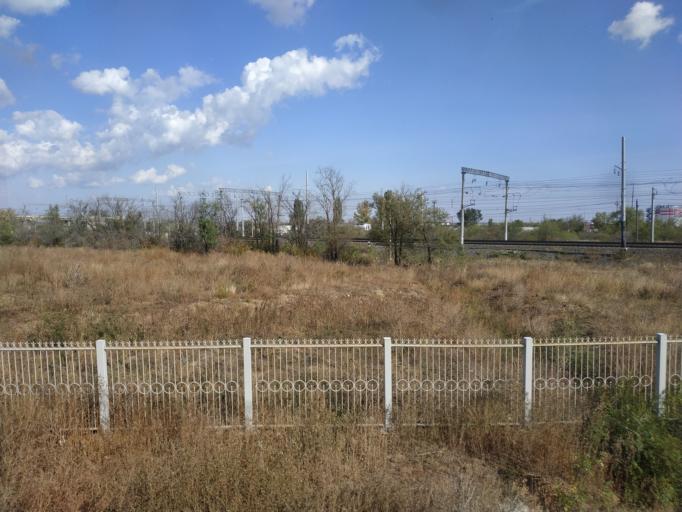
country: RU
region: Volgograd
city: Gumrak
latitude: 48.7937
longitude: 44.3636
